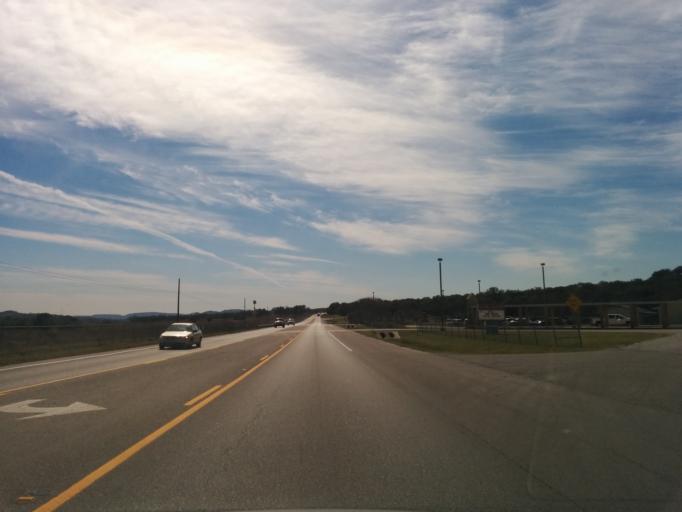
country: US
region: Texas
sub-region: Bexar County
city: Fair Oaks Ranch
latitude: 29.7290
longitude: -98.6235
